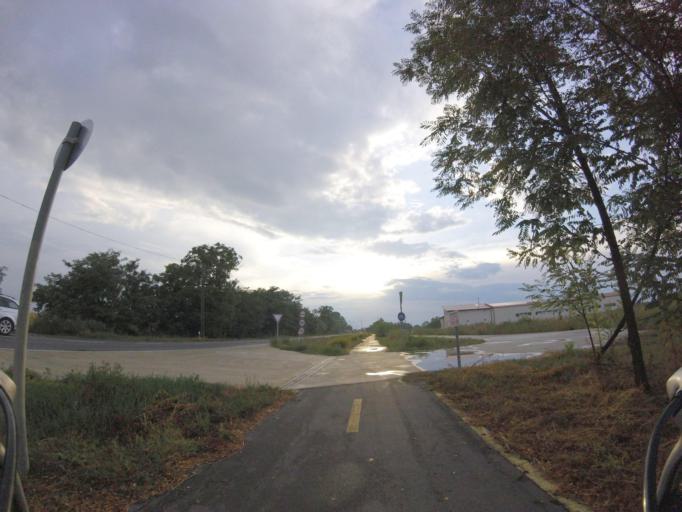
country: HU
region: Szabolcs-Szatmar-Bereg
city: Tunyogmatolcs
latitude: 47.9250
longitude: 22.4518
